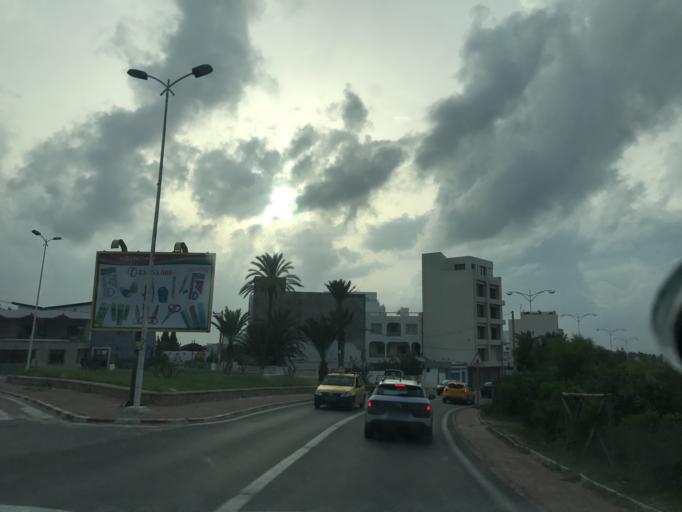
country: TN
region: Al Munastir
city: Saqanis
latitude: 35.7782
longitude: 10.7947
